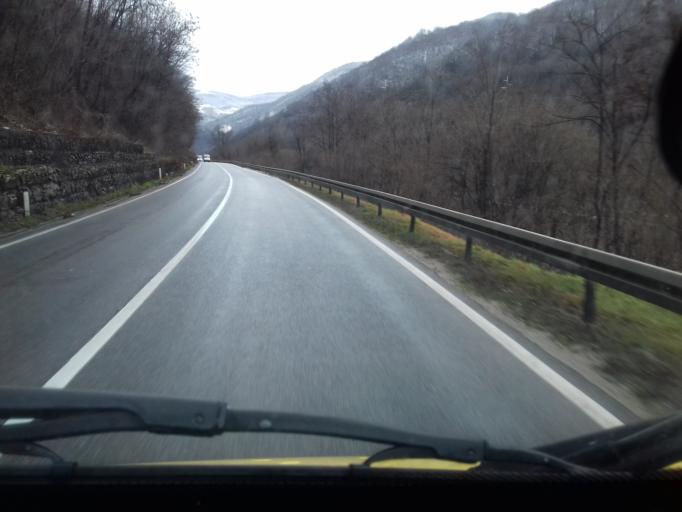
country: BA
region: Federation of Bosnia and Herzegovina
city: Lokvine
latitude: 44.2799
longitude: 17.8828
